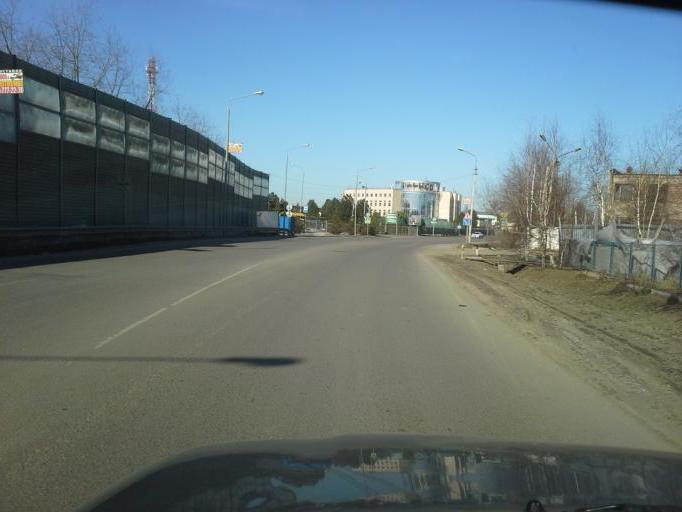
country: RU
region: Moskovskaya
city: Odintsovo
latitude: 55.6579
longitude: 37.2488
